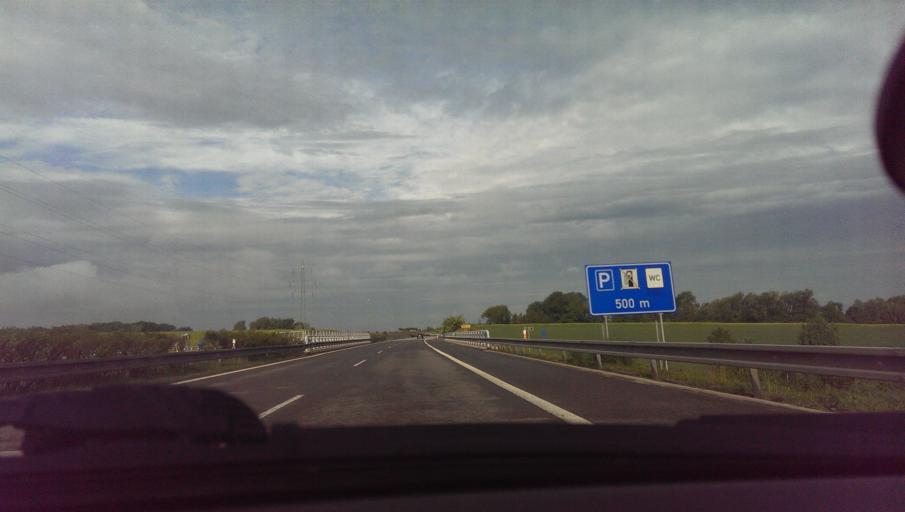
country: CZ
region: Olomoucky
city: Kojetin
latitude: 49.3208
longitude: 17.2744
